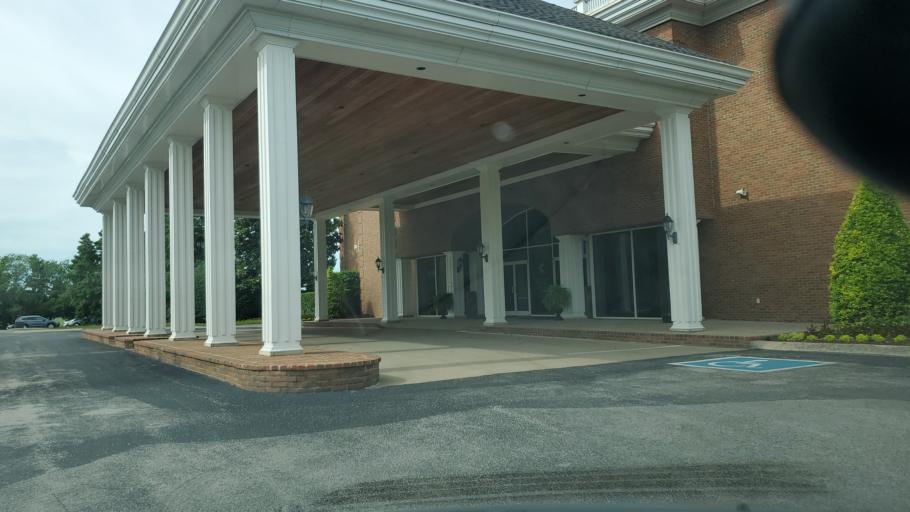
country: US
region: Tennessee
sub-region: Davidson County
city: Lakewood
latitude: 36.2201
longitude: -86.6805
